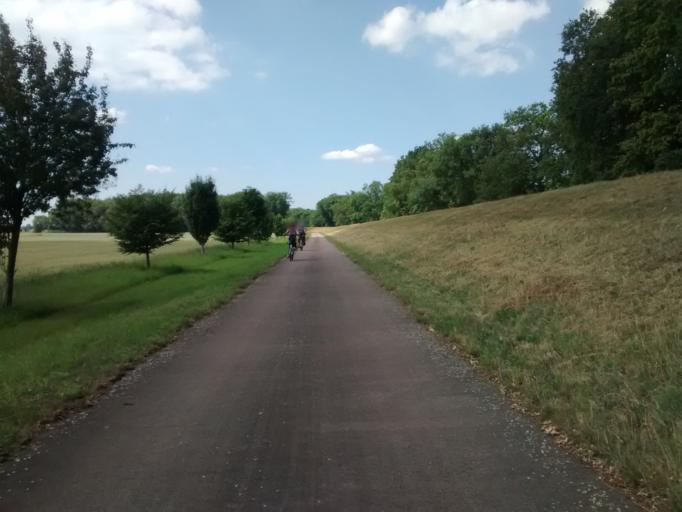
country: DE
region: Saxony-Anhalt
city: Bergwitz
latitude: 51.8492
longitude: 12.5273
